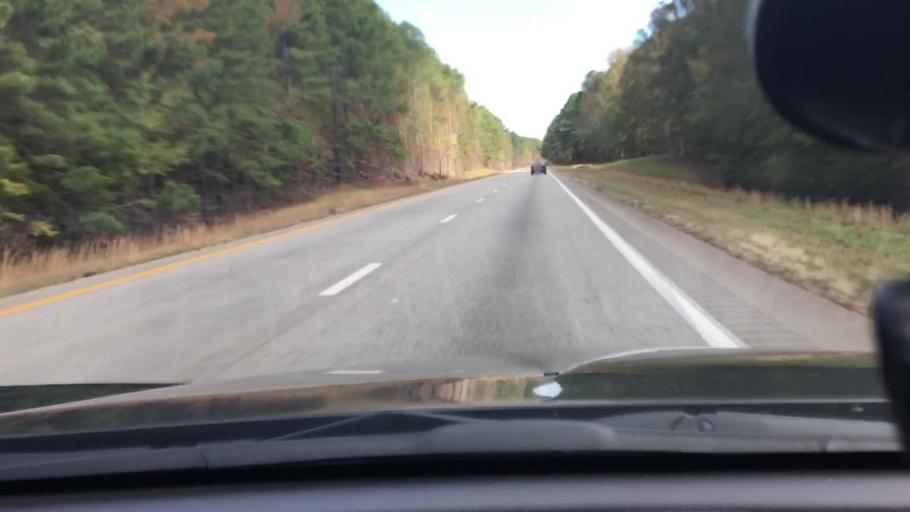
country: US
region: North Carolina
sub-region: Wake County
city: Zebulon
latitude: 35.7944
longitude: -78.1666
